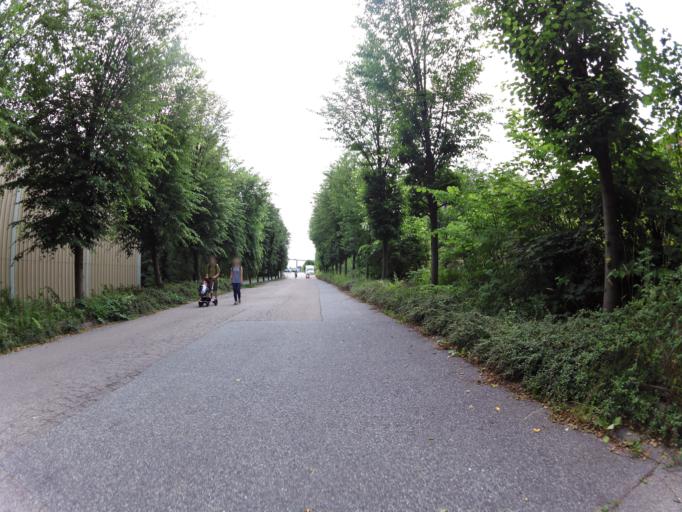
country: NO
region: Ostfold
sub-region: Fredrikstad
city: Fredrikstad
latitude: 59.2168
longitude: 10.9621
